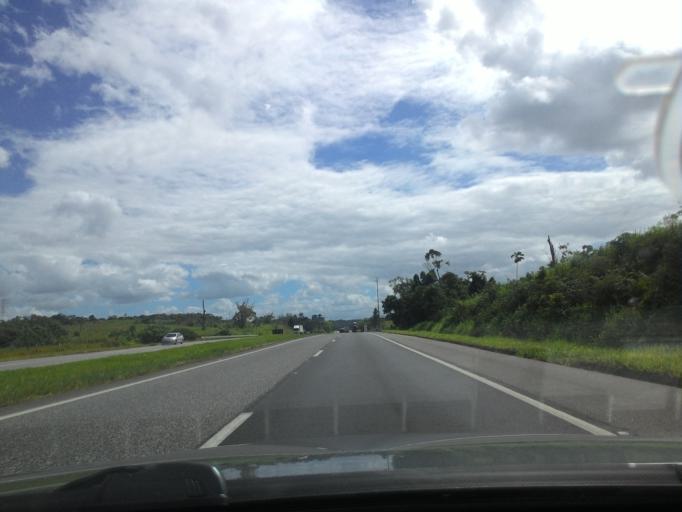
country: BR
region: Sao Paulo
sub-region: Pariquera-Acu
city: Pariquera Acu
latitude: -24.6337
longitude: -47.9076
